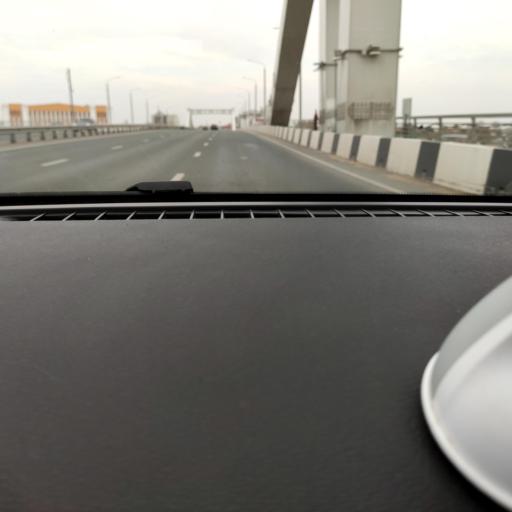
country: RU
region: Samara
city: Rozhdestveno
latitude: 53.1737
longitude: 50.0857
